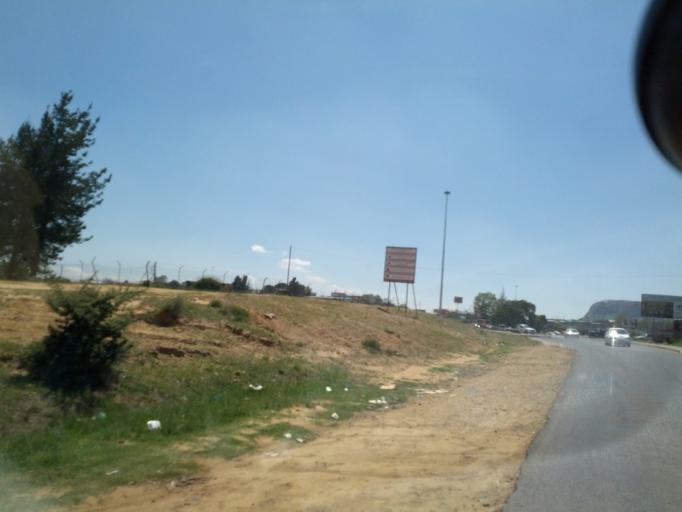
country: LS
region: Butha-Buthe
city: Butha-Buthe
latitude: -28.7722
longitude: 28.2441
